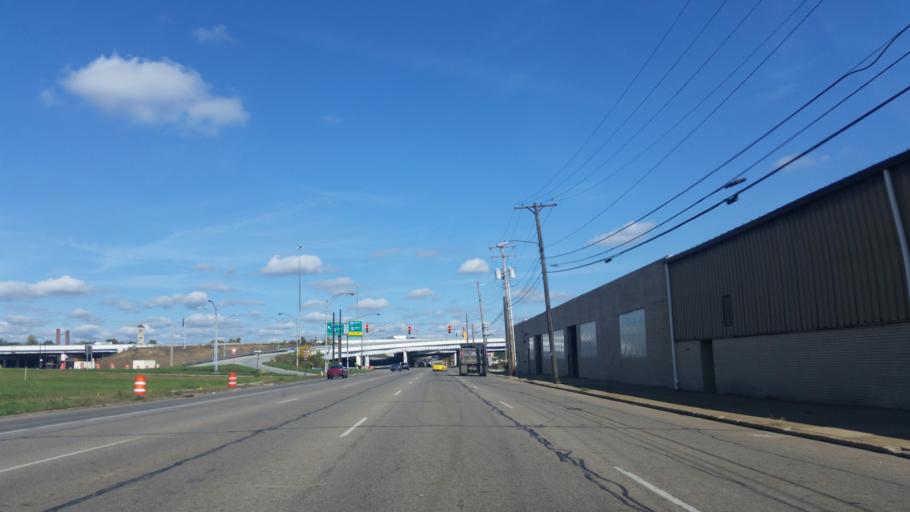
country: US
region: Ohio
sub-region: Summit County
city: Akron
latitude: 41.0599
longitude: -81.5269
